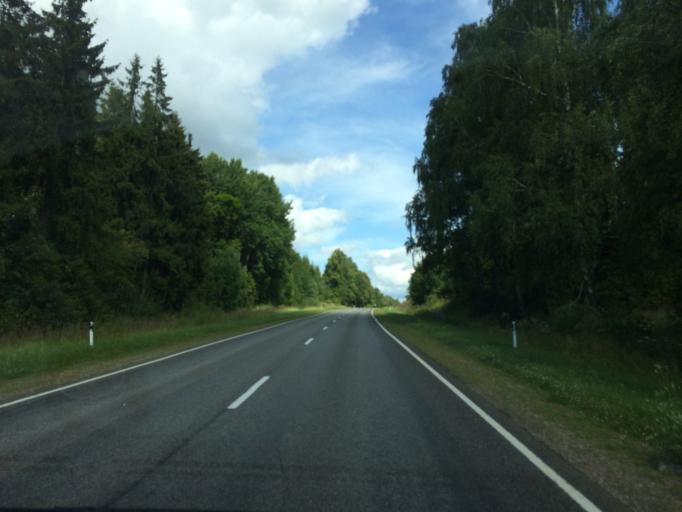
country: LV
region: Rezekne
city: Rezekne
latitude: 56.6274
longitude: 27.4616
